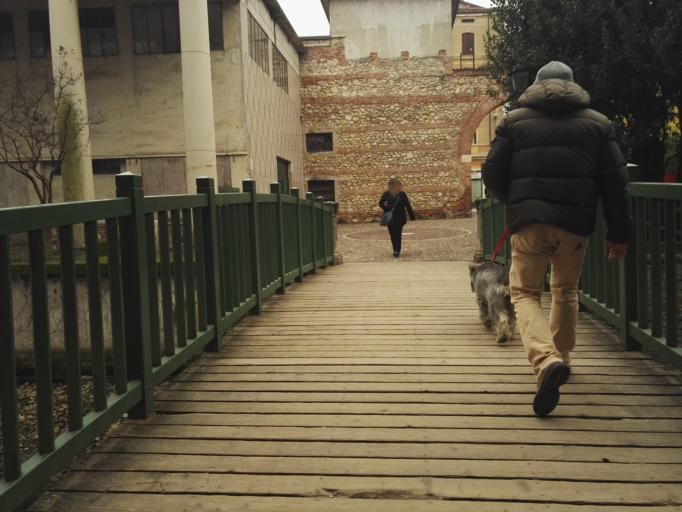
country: IT
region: Veneto
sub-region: Provincia di Vicenza
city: Vicenza
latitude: 45.5467
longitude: 11.5399
